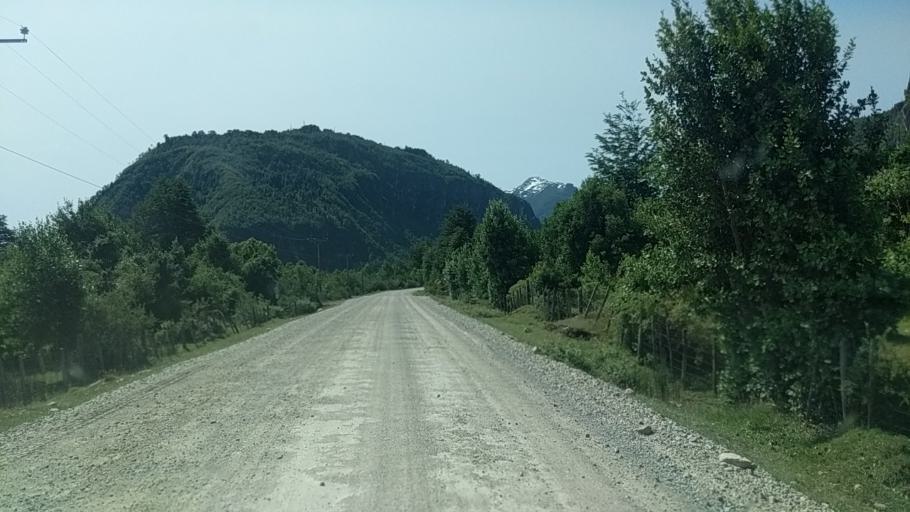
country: CL
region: Los Lagos
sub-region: Provincia de Palena
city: Palena
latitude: -43.4663
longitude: -72.1149
